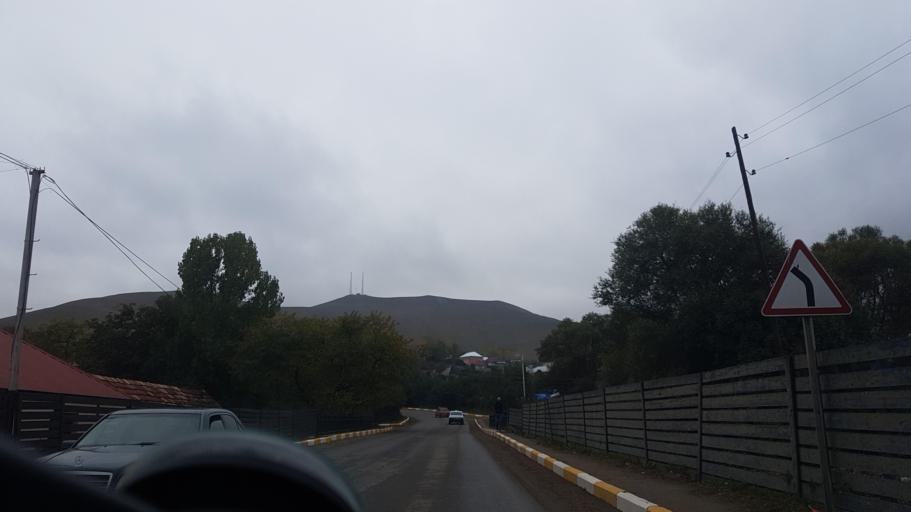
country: AZ
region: Gadabay Rayon
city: Ariqdam
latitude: 40.6573
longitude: 45.8073
